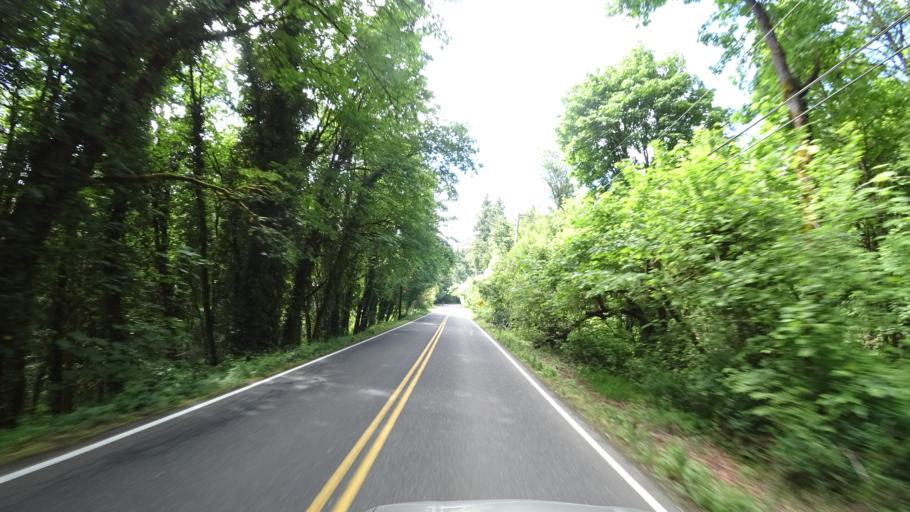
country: US
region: Oregon
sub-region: Washington County
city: Oak Hills
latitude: 45.5937
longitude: -122.8173
